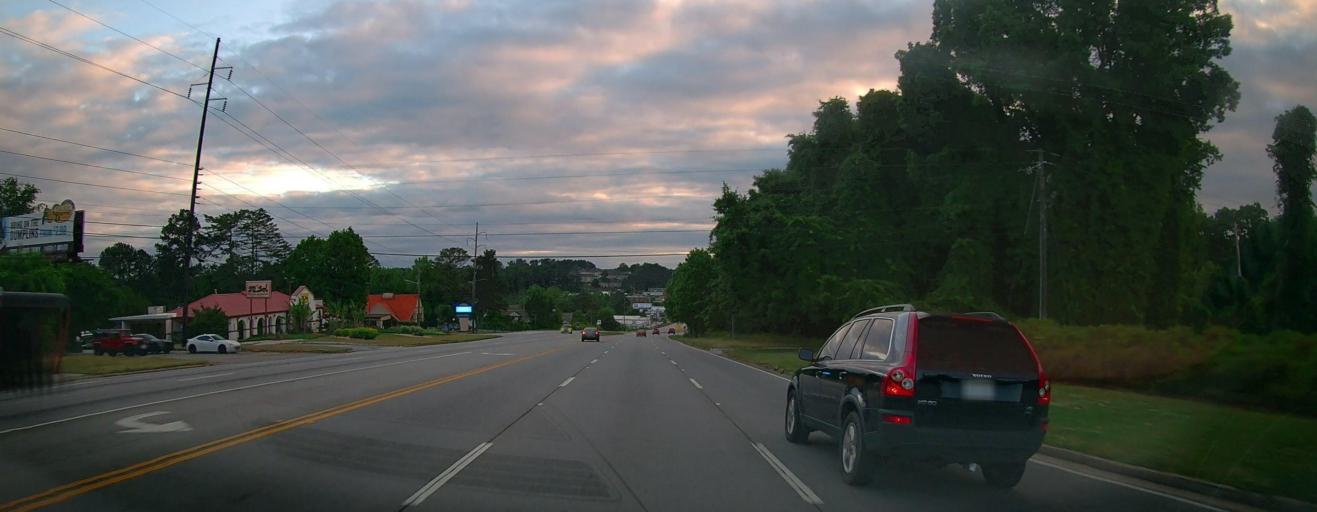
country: US
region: Georgia
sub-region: Clarke County
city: Athens
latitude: 33.9479
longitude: -83.4179
